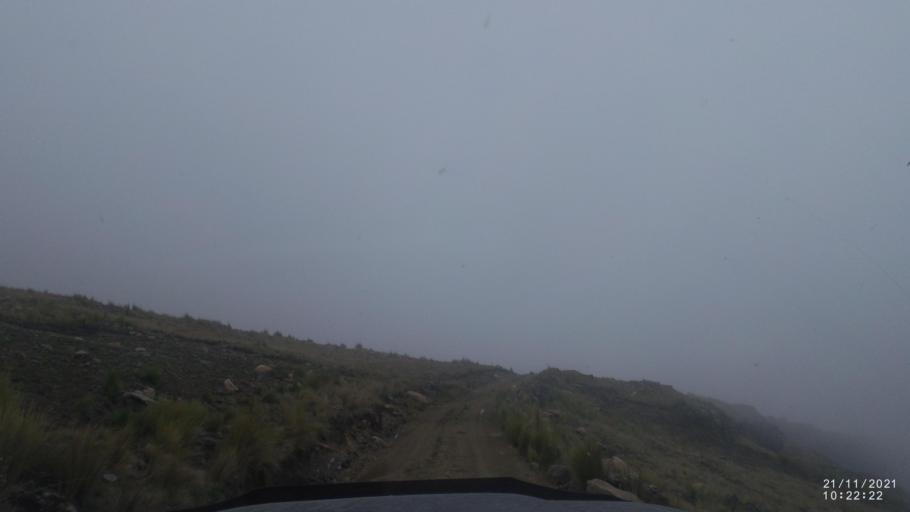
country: BO
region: Cochabamba
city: Cochabamba
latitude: -16.9848
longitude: -66.2609
